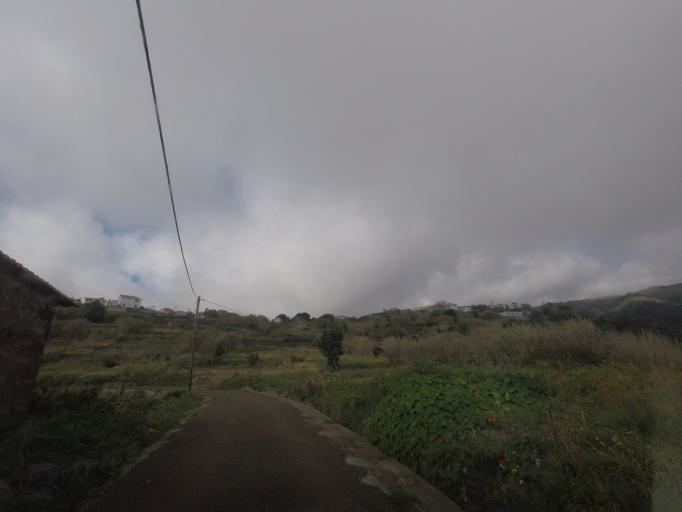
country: PT
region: Madeira
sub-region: Calheta
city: Faja da Ovelha
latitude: 32.7627
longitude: -17.2169
